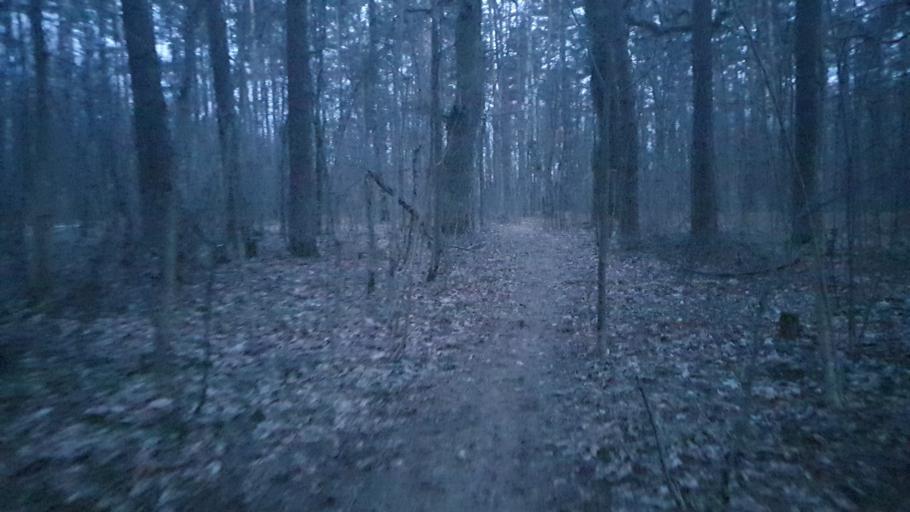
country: LV
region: Marupe
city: Marupe
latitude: 56.9360
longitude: 24.0186
